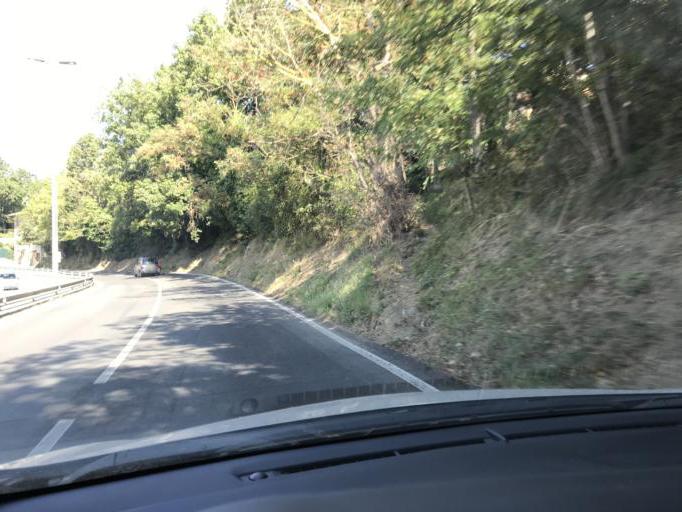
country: IT
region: Umbria
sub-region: Provincia di Perugia
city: Ponte Felcino
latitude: 43.1074
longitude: 12.4309
